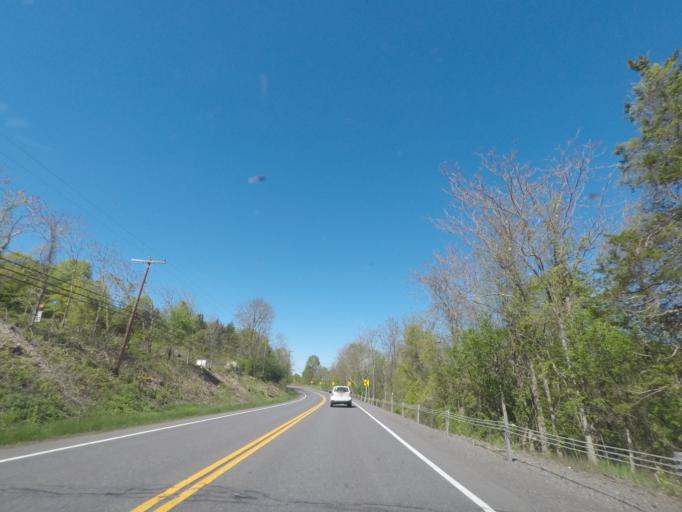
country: US
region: New York
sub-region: Greene County
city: Jefferson Heights
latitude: 42.2552
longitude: -73.8595
